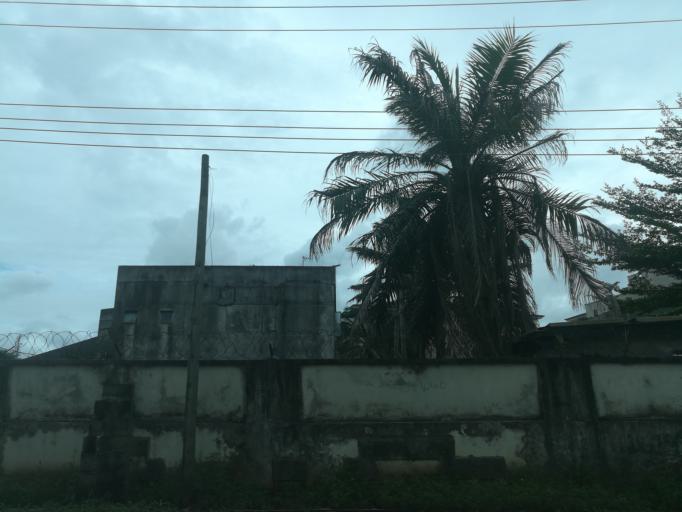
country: NG
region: Lagos
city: Lagos
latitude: 6.4357
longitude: 3.4134
